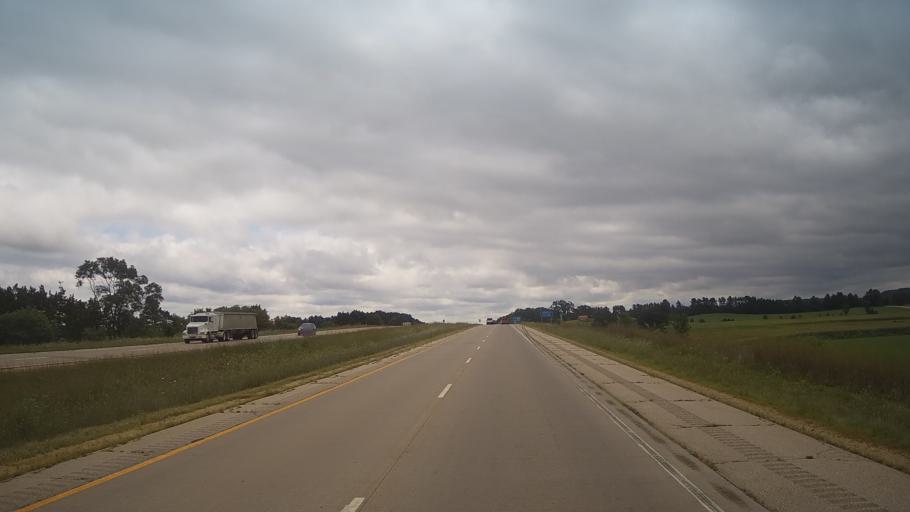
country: US
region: Wisconsin
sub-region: Monroe County
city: Sparta
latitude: 43.9161
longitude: -90.8449
